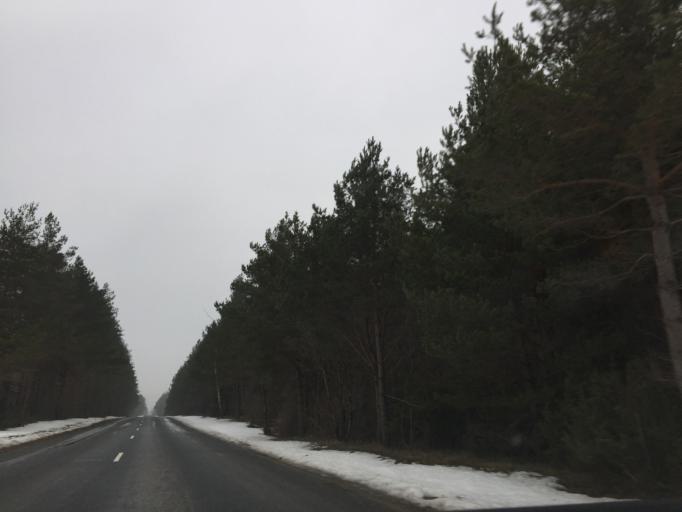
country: EE
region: Saare
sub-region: Orissaare vald
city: Orissaare
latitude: 58.3949
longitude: 22.8244
